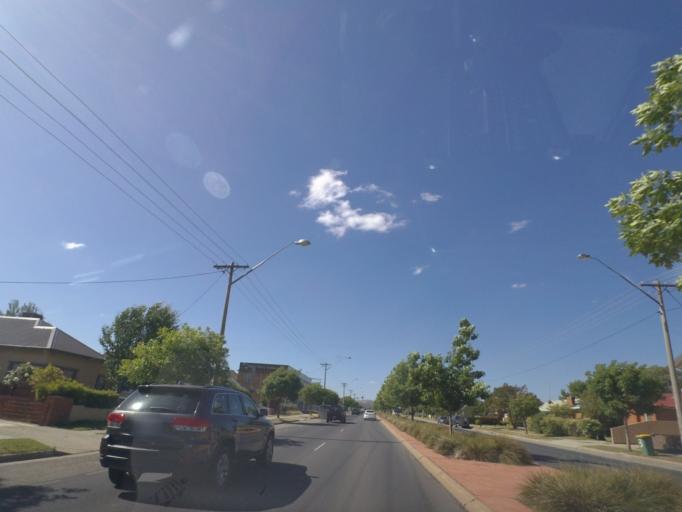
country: AU
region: New South Wales
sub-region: Albury Municipality
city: North Albury
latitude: -36.0620
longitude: 146.9317
